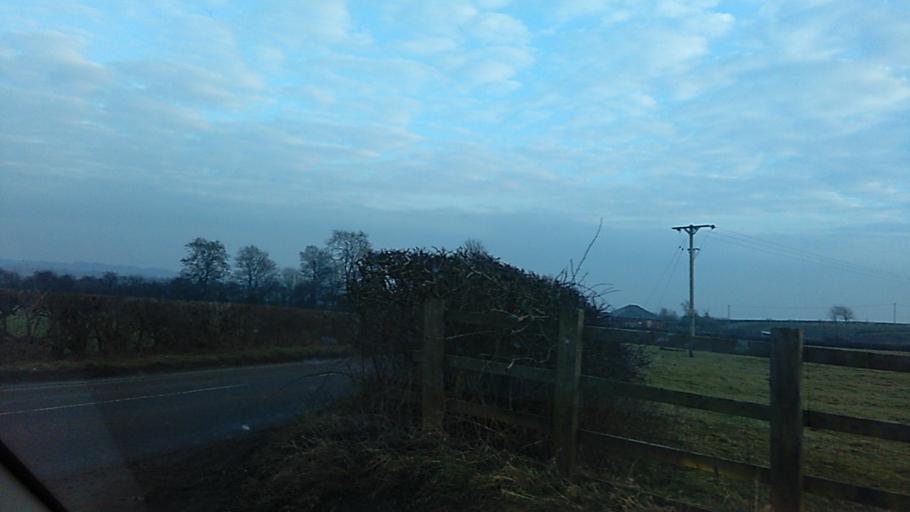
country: GB
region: England
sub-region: Leicestershire
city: Melton Mowbray
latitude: 52.8197
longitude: -0.8787
